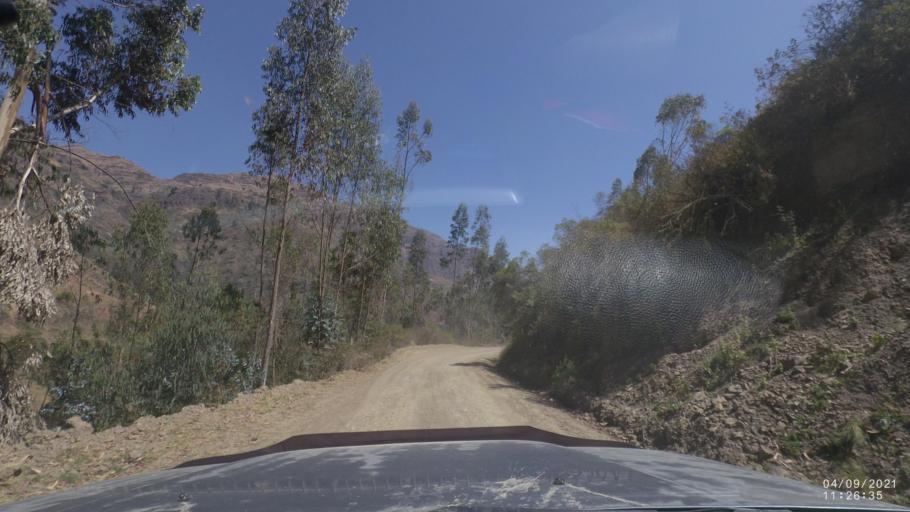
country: BO
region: Cochabamba
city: Colchani
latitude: -17.2525
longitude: -66.5141
